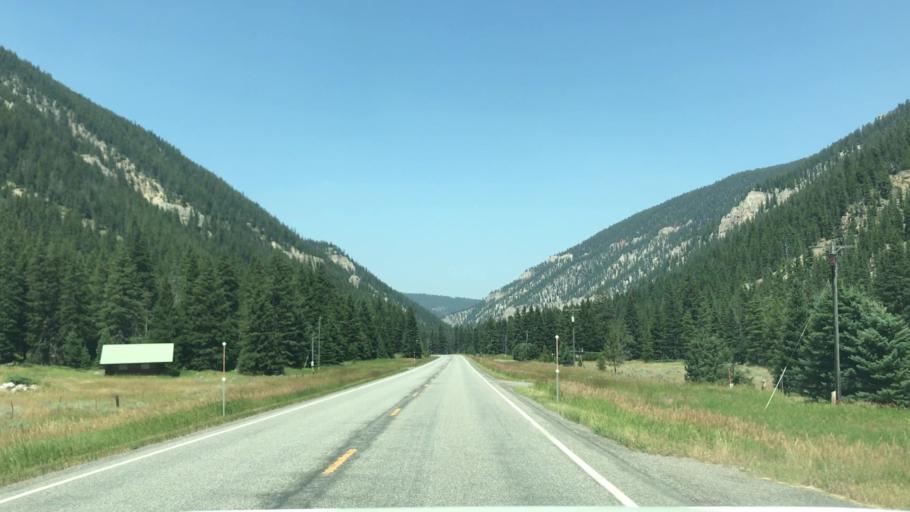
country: US
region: Montana
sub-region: Gallatin County
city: Big Sky
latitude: 45.1219
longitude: -111.2288
